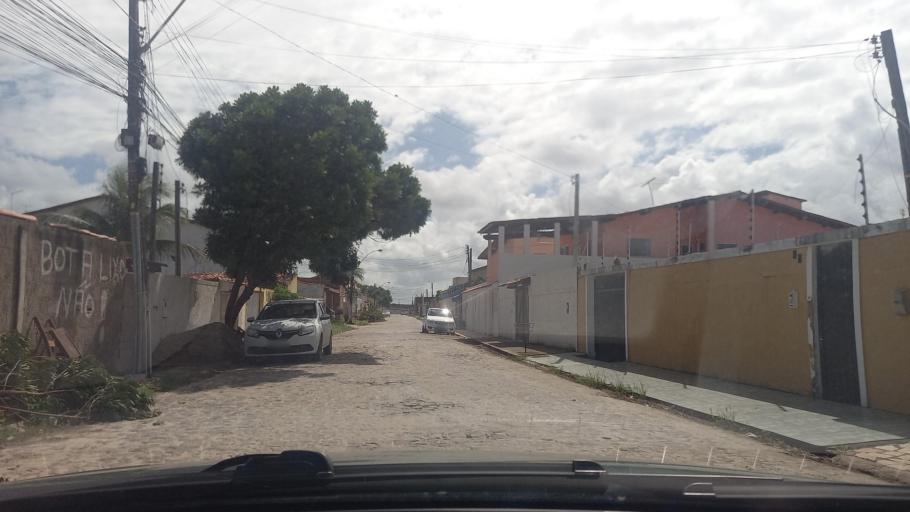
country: BR
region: Alagoas
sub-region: Marechal Deodoro
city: Marechal Deodoro
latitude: -9.7668
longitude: -35.8476
